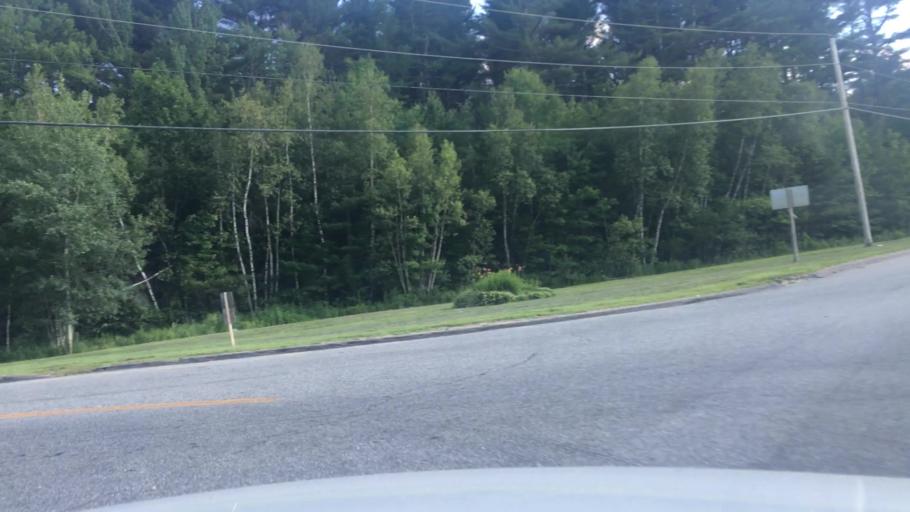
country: US
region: Maine
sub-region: Androscoggin County
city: Livermore
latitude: 44.3904
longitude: -70.2311
